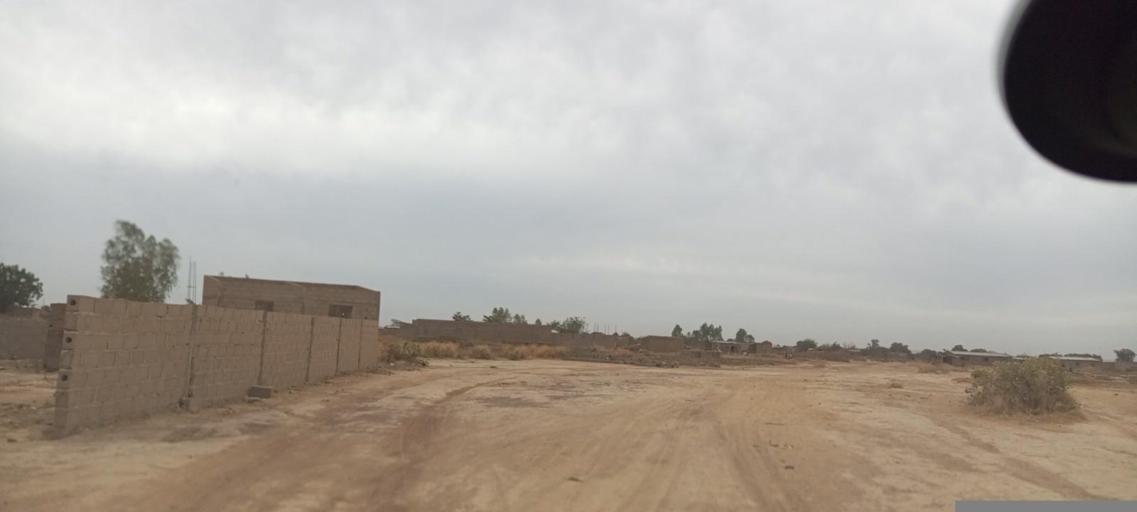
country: ML
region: Koulikoro
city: Kati
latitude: 12.7990
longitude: -8.2487
